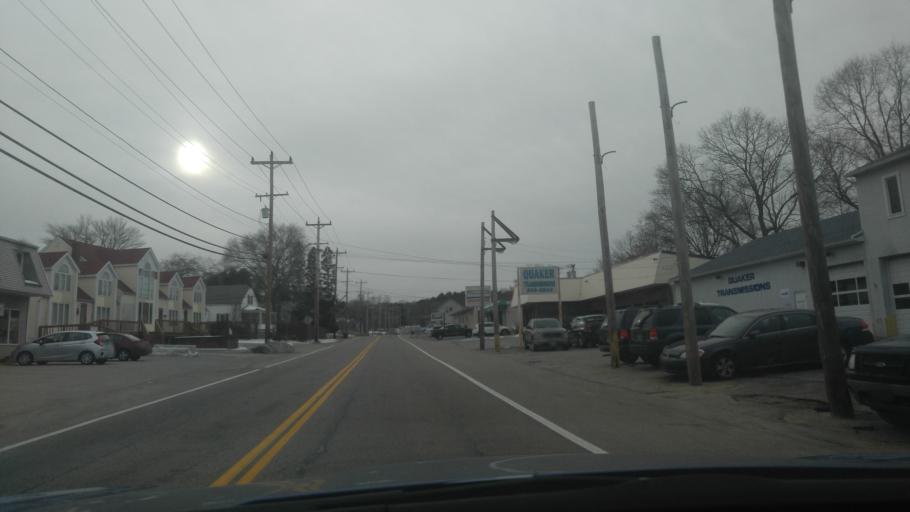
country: US
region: Rhode Island
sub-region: Kent County
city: West Warwick
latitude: 41.6802
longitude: -71.5308
